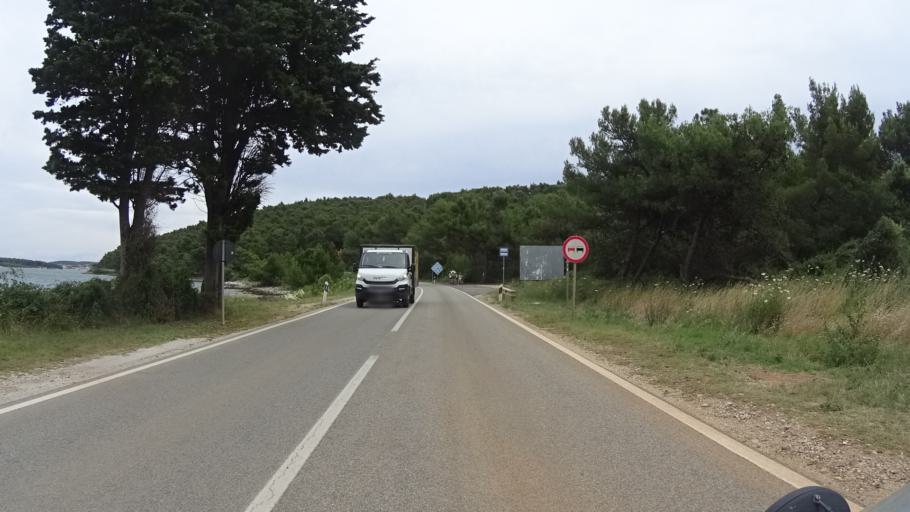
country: HR
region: Istarska
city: Medulin
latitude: 44.8152
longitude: 13.9003
